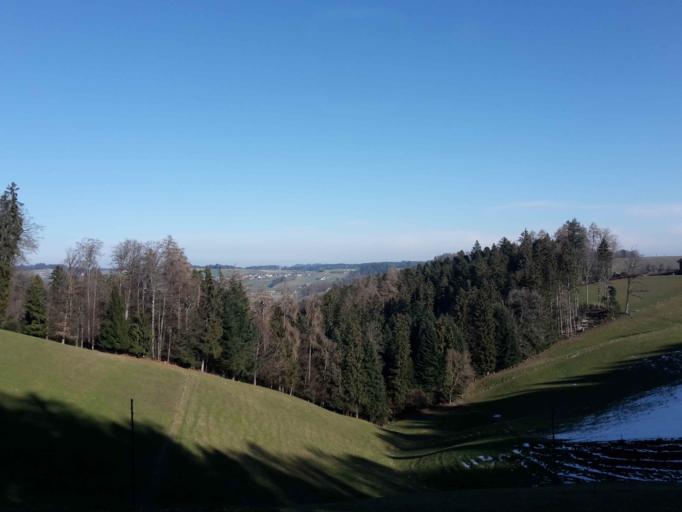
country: CH
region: Bern
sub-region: Oberaargau
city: Rohrbach
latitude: 47.1252
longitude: 7.7950
